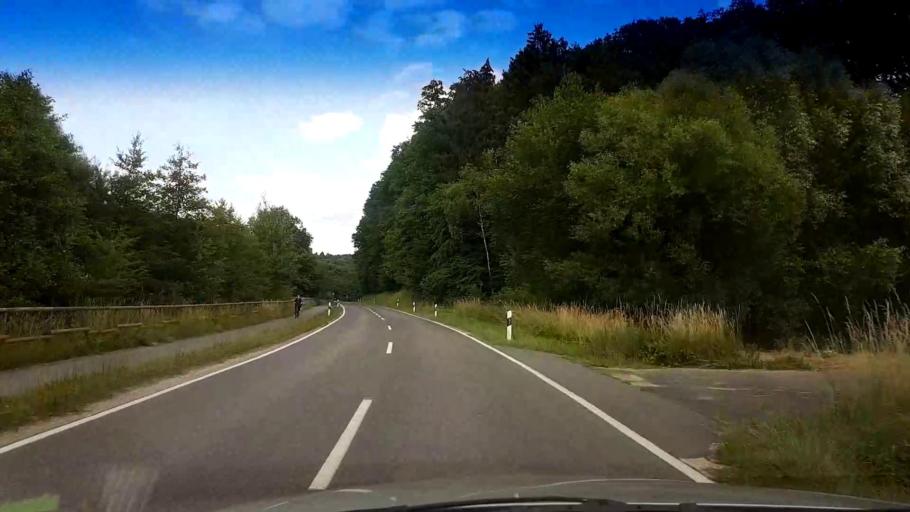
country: DE
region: Bavaria
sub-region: Upper Franconia
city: Gerach
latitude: 50.0021
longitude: 10.8001
